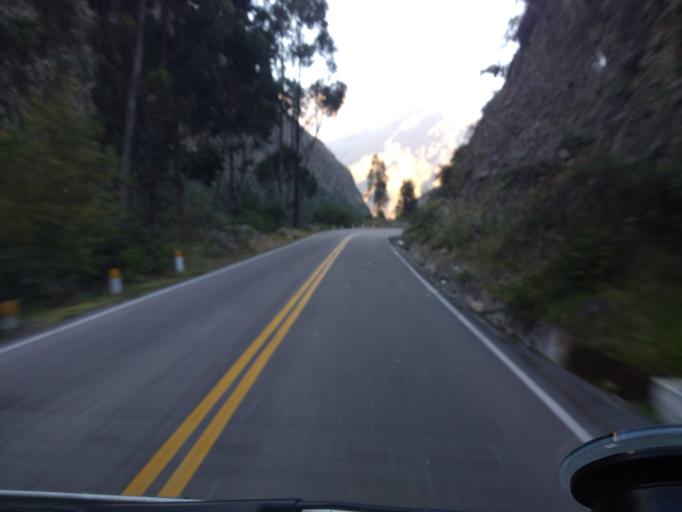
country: PE
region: Cusco
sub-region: Provincia de Urubamba
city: Ollantaytambo
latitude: -13.1987
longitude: -72.2947
